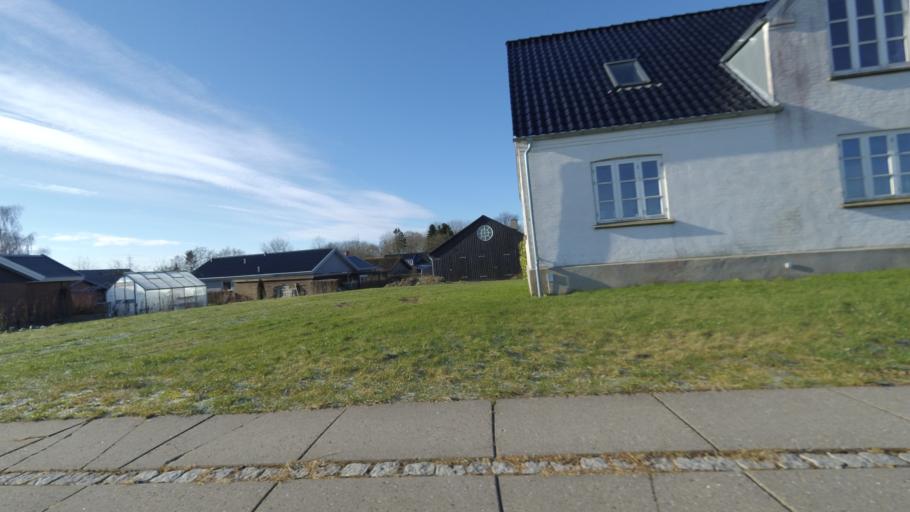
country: DK
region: Central Jutland
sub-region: Arhus Kommune
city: Kolt
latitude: 56.1240
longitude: 10.0648
